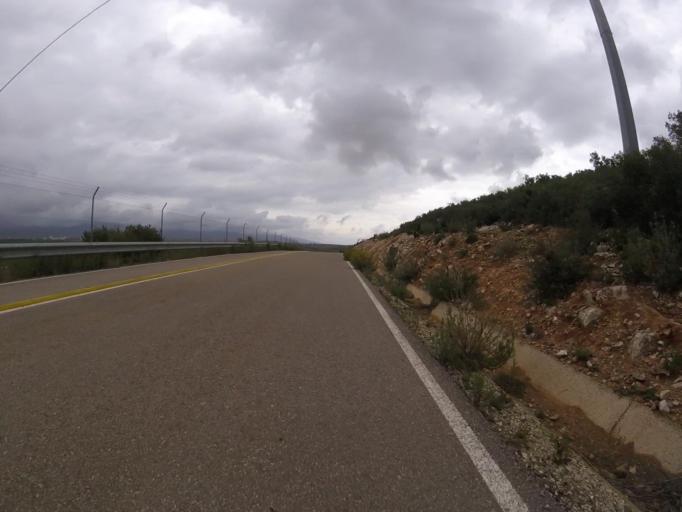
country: ES
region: Valencia
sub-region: Provincia de Castello
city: Benlloch
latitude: 40.1887
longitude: 0.0478
